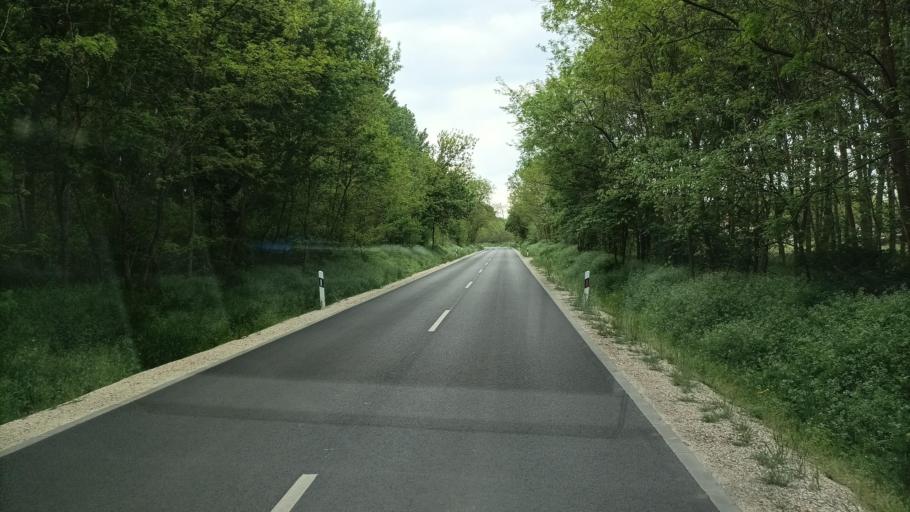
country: HU
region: Pest
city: Nyaregyhaza
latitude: 47.2847
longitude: 19.4596
